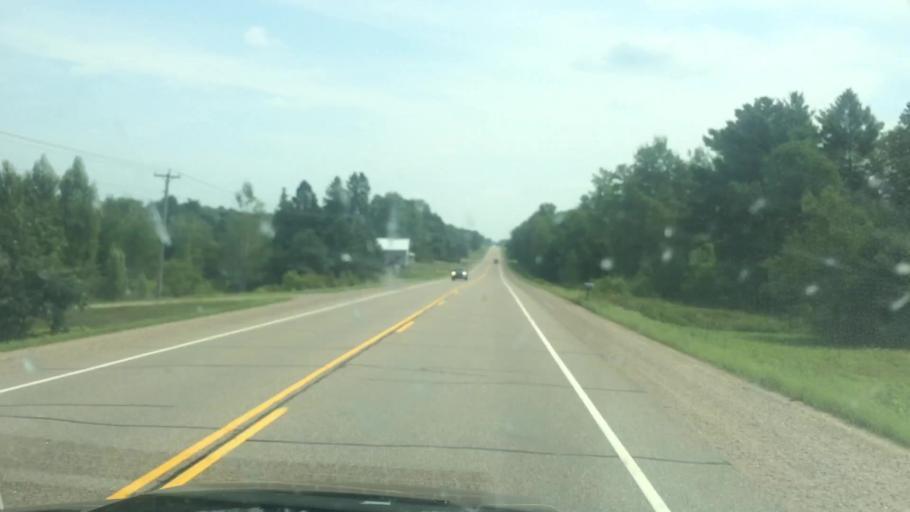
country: US
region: Wisconsin
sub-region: Langlade County
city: Antigo
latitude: 45.1686
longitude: -88.9603
